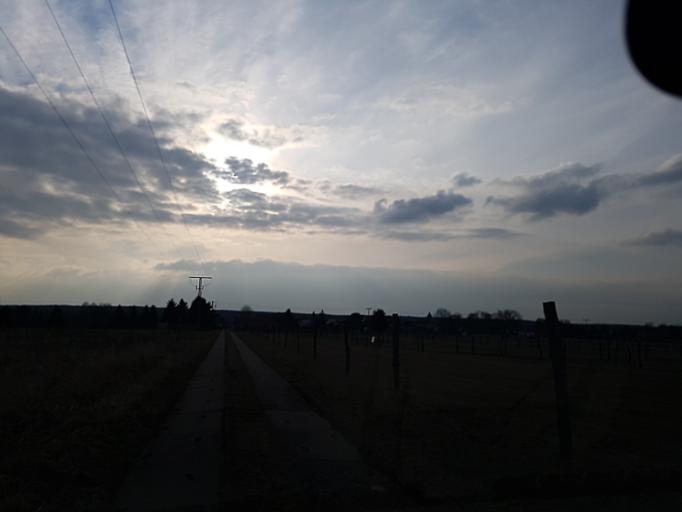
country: DE
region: Brandenburg
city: Wollin
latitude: 52.2501
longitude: 12.4914
